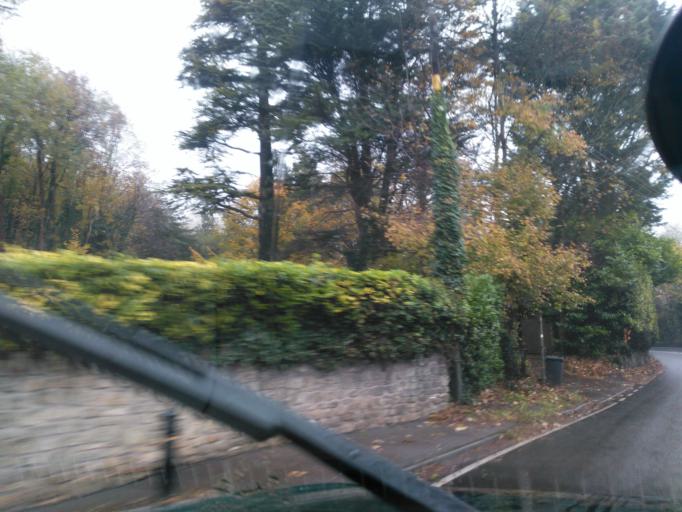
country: GB
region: England
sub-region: Bath and North East Somerset
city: Freshford
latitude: 51.3475
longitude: -2.3181
